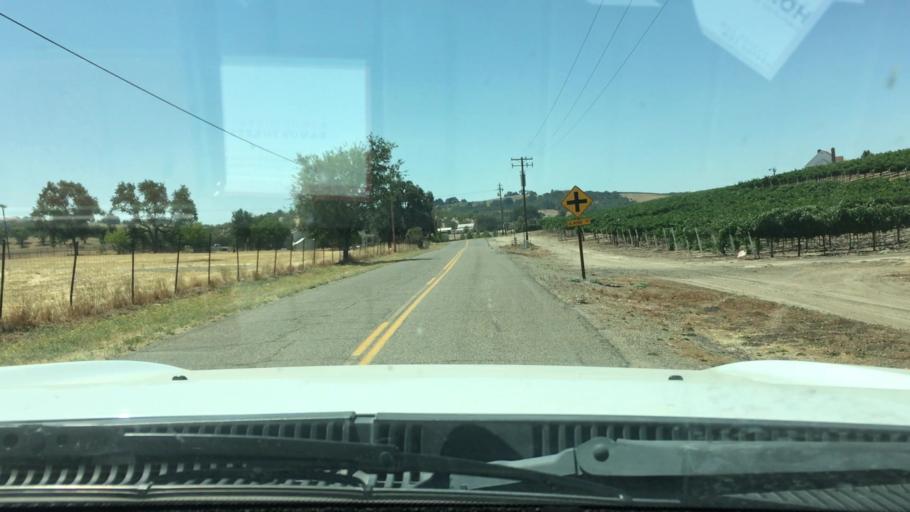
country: US
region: California
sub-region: San Luis Obispo County
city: Atascadero
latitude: 35.5408
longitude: -120.6105
